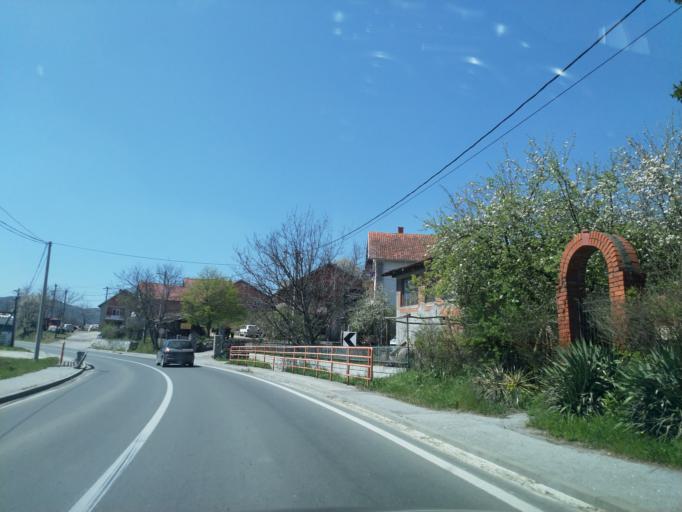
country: RS
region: Central Serbia
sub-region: Sumadijski Okrug
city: Arangelovac
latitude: 44.3355
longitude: 20.4873
